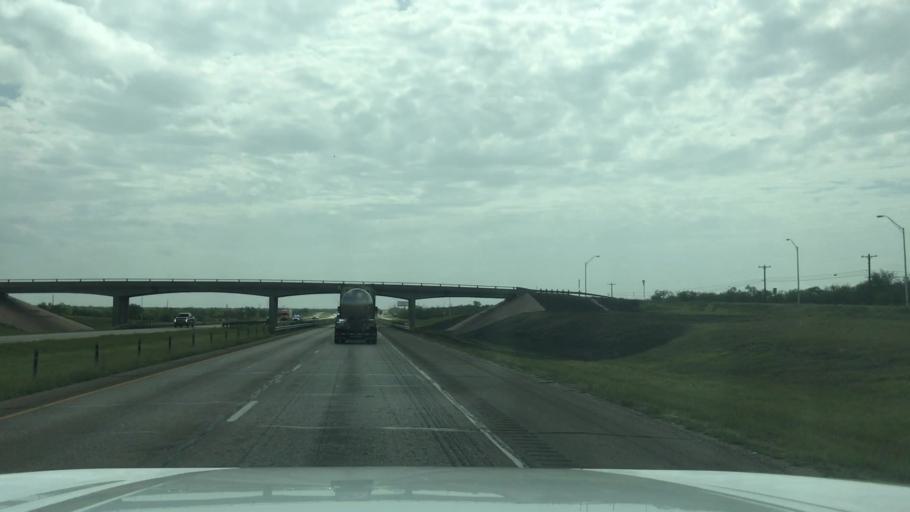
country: US
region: Texas
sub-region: Taylor County
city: Potosi
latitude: 32.4323
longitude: -99.6065
